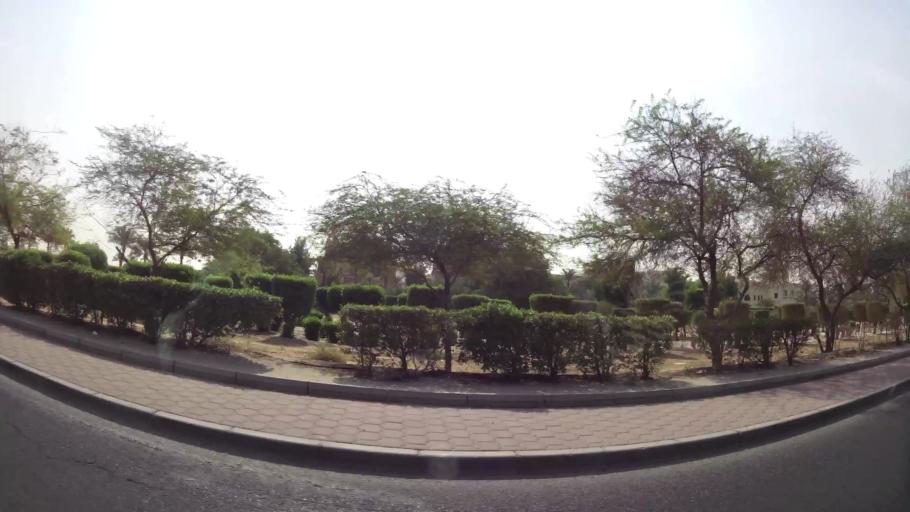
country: KW
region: Al Asimah
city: Ar Rabiyah
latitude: 29.3065
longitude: 47.8986
